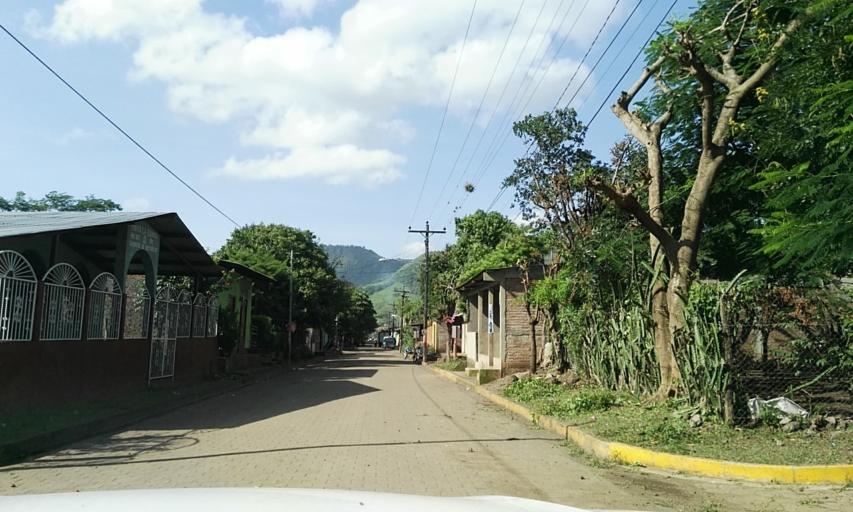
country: NI
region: Matagalpa
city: Terrabona
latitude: 12.7323
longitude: -85.9643
